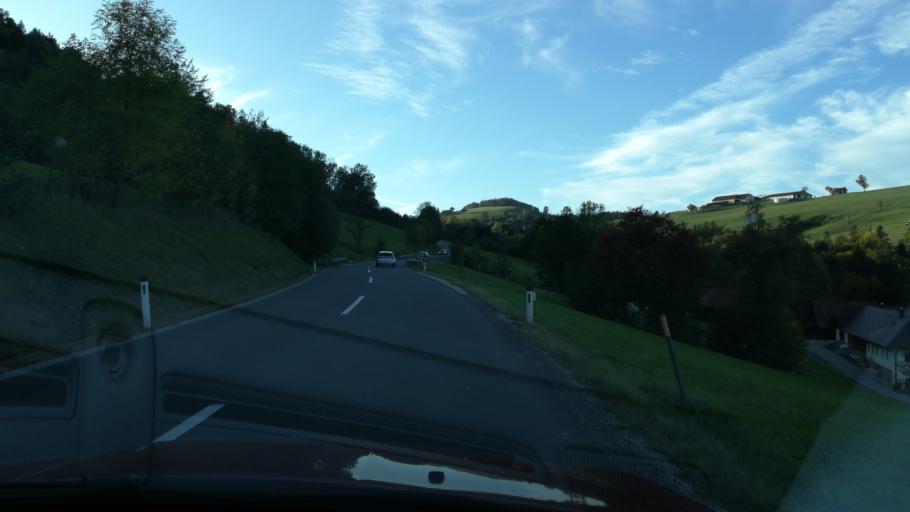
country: AT
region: Upper Austria
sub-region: Politischer Bezirk Steyr-Land
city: Ternberg
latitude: 47.9618
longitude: 14.3134
